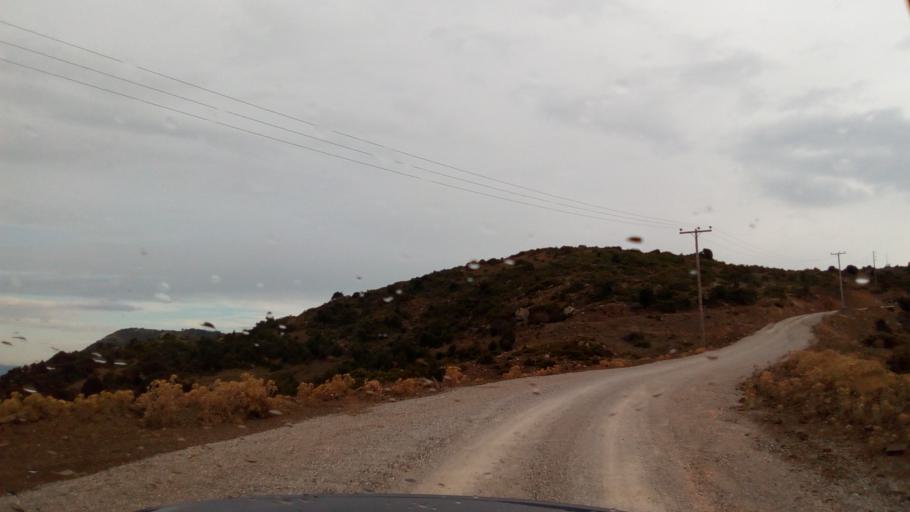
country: GR
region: West Greece
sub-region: Nomos Achaias
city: Kamarai
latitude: 38.4350
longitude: 22.0557
